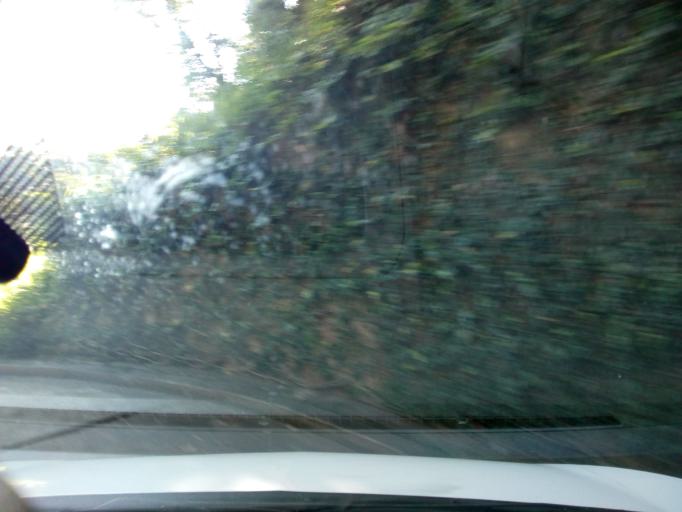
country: BR
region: Rio de Janeiro
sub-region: Rio De Janeiro
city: Rio de Janeiro
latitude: -22.9889
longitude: -43.2296
